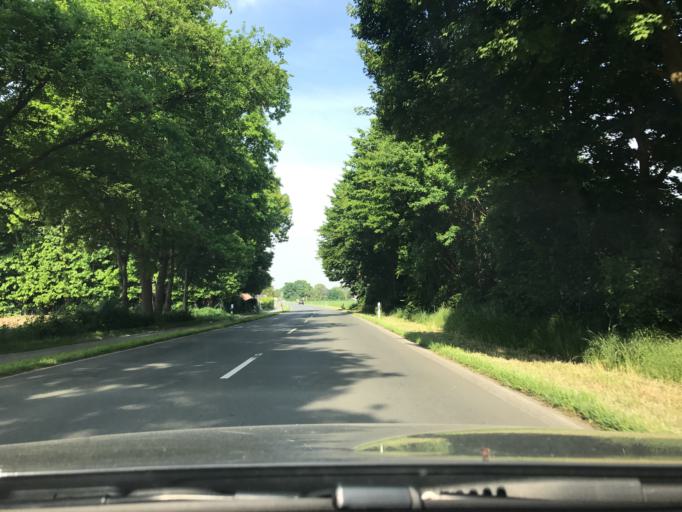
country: DE
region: North Rhine-Westphalia
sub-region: Regierungsbezirk Dusseldorf
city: Rheurdt
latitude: 51.4415
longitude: 6.4680
